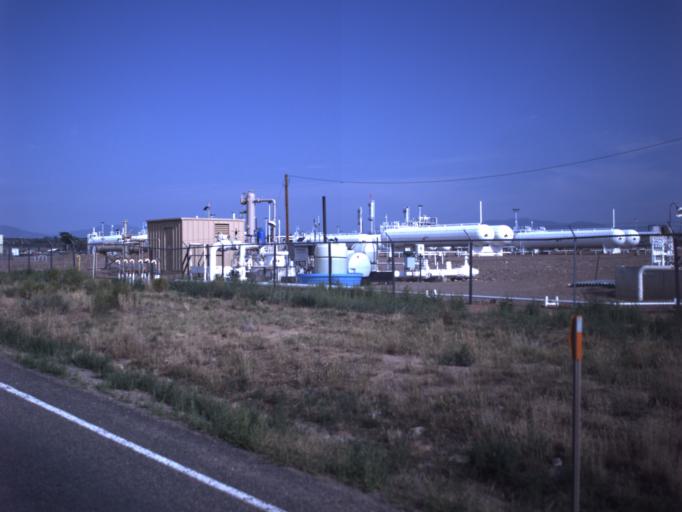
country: US
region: Utah
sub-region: Duchesne County
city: Duchesne
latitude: 40.3557
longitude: -110.3246
